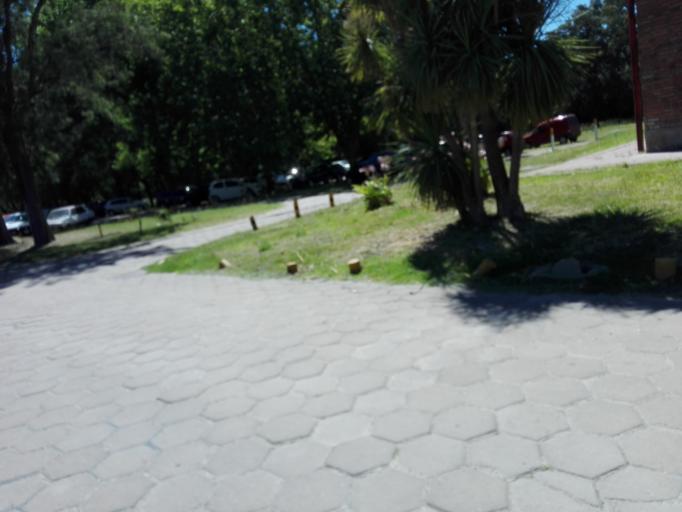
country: AR
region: Buenos Aires
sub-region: Partido de La Plata
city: La Plata
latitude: -34.8993
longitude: -57.9290
